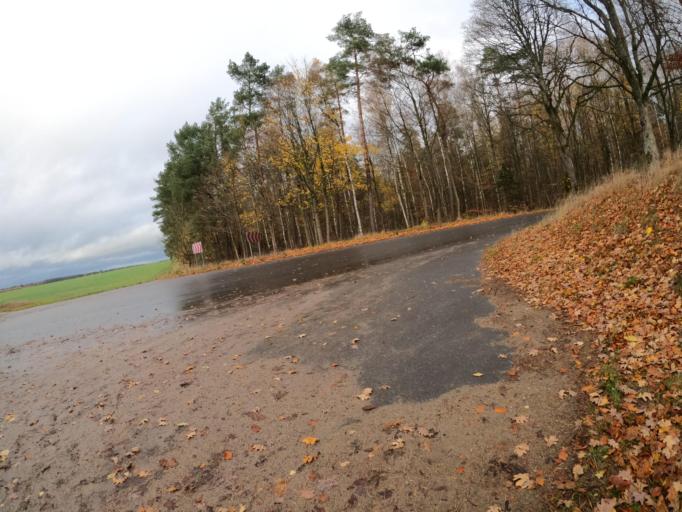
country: PL
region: West Pomeranian Voivodeship
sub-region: Powiat walecki
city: Tuczno
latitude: 53.2341
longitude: 16.2533
